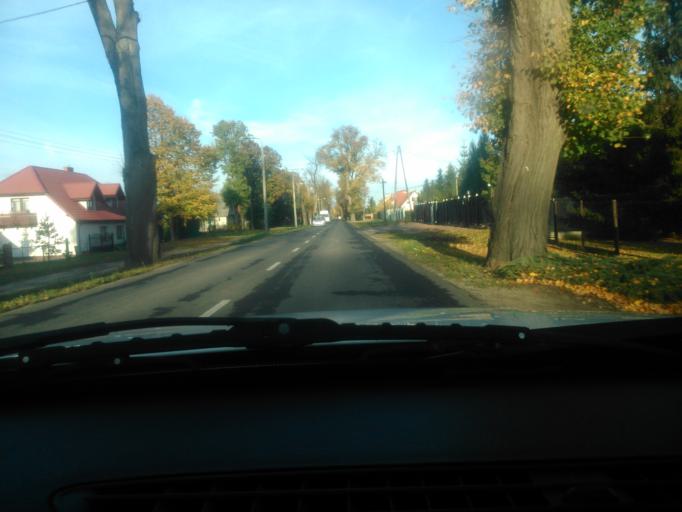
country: PL
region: Kujawsko-Pomorskie
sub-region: Powiat golubsko-dobrzynski
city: Kowalewo Pomorskie
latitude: 53.1575
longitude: 18.8875
